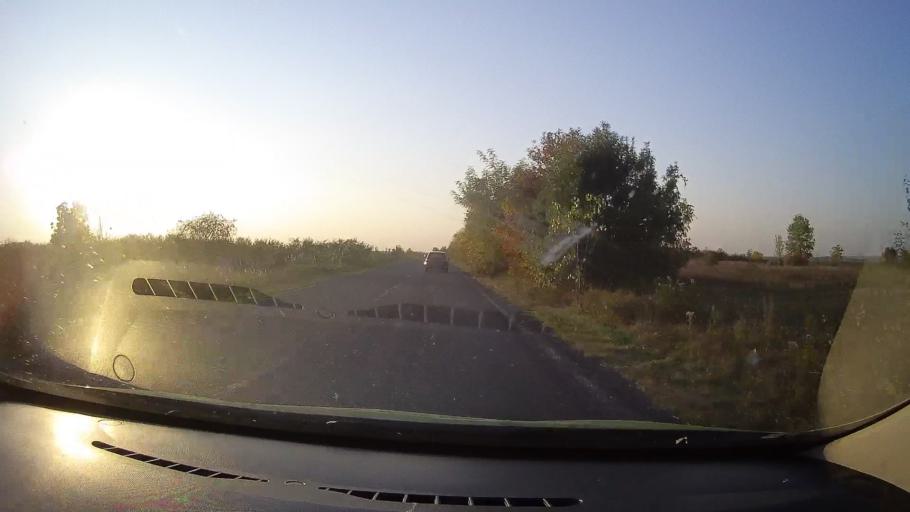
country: RO
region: Arad
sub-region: Comuna Bocsig
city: Bocsig
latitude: 46.4185
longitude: 21.9785
